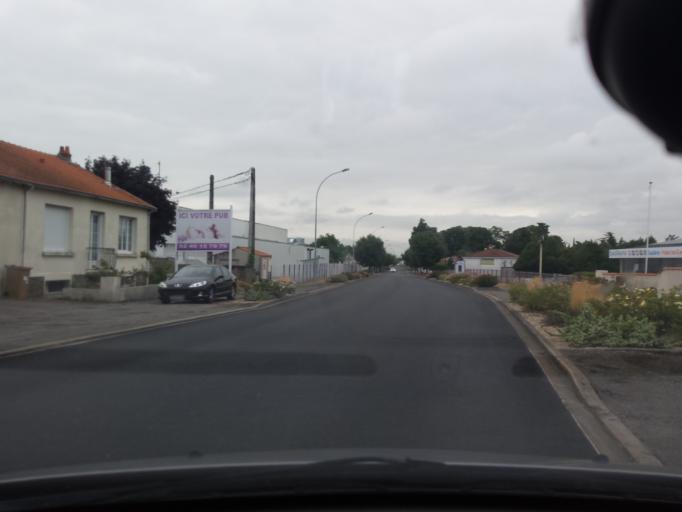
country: FR
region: Pays de la Loire
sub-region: Departement de la Vendee
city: Lucon
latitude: 46.4674
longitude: -1.1741
